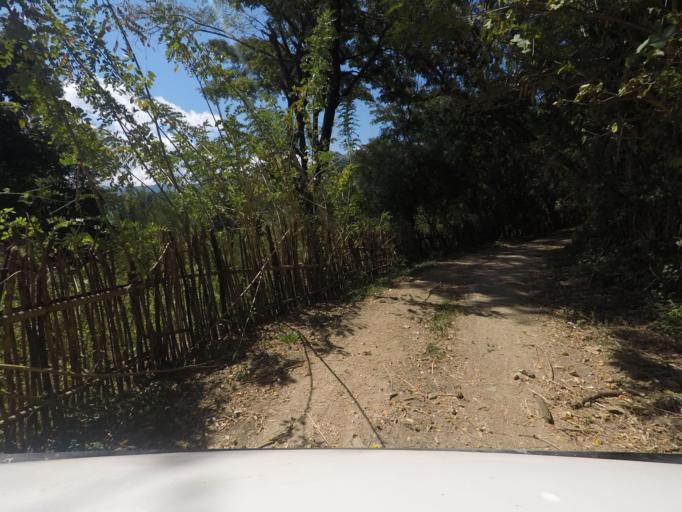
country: TL
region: Ermera
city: Gleno
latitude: -8.7193
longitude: 125.3034
